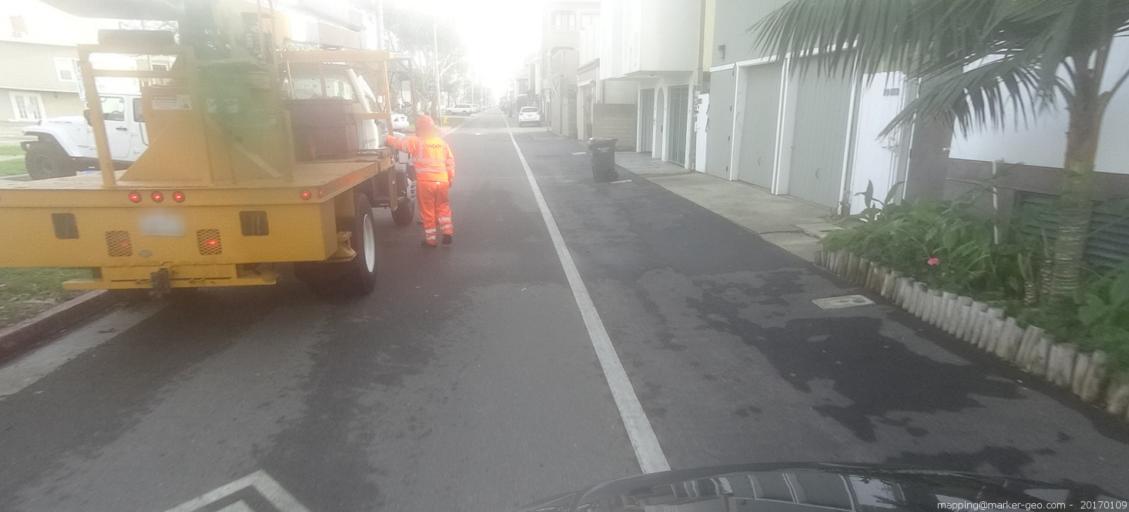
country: US
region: California
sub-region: Orange County
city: Seal Beach
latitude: 33.7230
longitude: -118.0774
